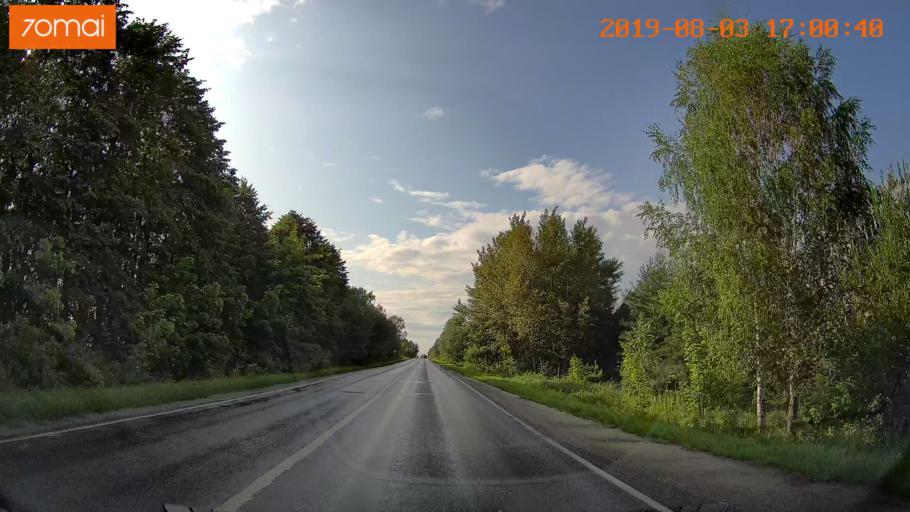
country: RU
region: Moskovskaya
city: Voskresensk
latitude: 55.3387
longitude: 38.6151
